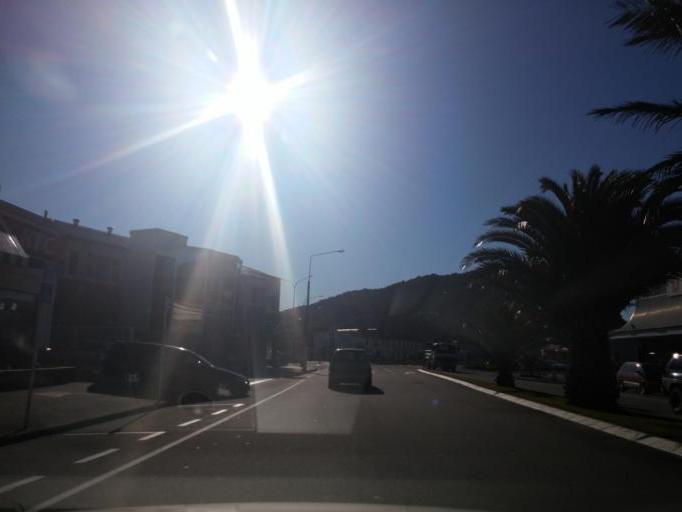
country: NZ
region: West Coast
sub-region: Grey District
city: Greymouth
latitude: -42.4510
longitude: 171.2103
